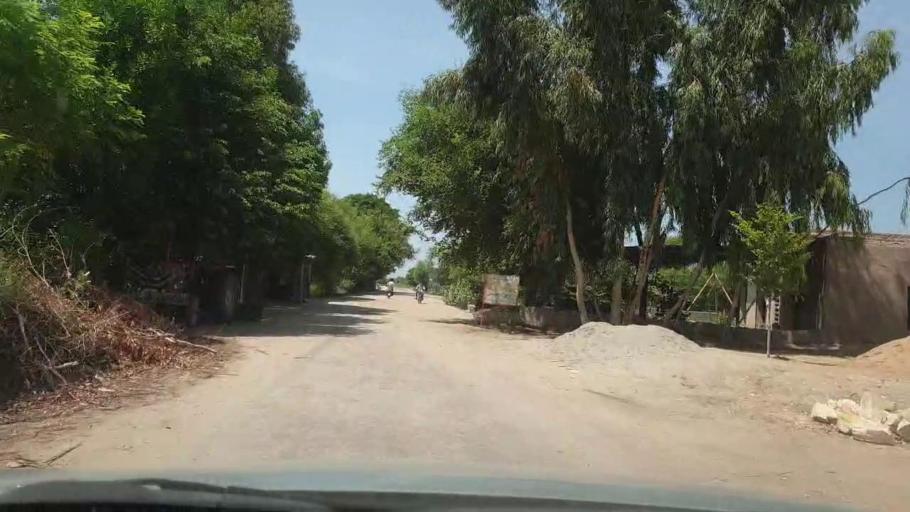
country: PK
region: Sindh
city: Pano Aqil
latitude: 27.6910
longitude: 69.1107
